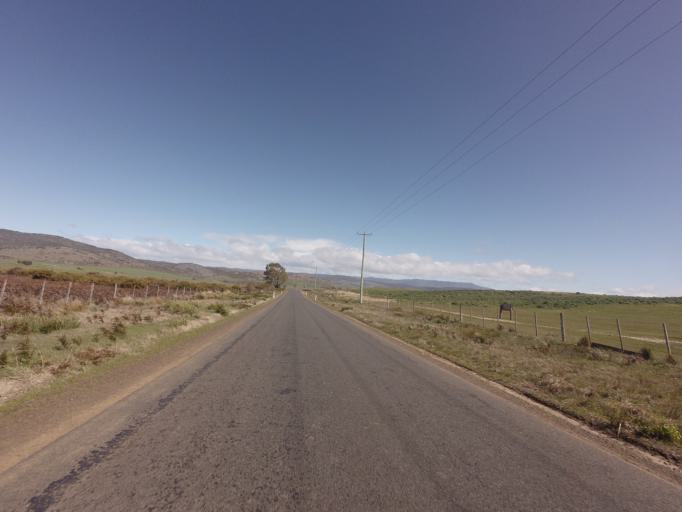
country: AU
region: Tasmania
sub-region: Northern Midlands
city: Evandale
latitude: -41.9008
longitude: 147.4029
